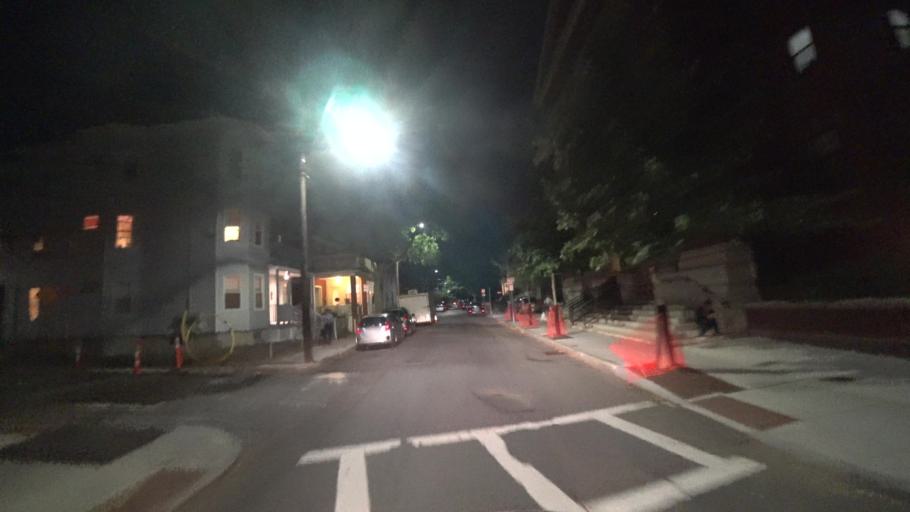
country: US
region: Massachusetts
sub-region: Middlesex County
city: Cambridge
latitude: 42.3605
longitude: -71.1071
